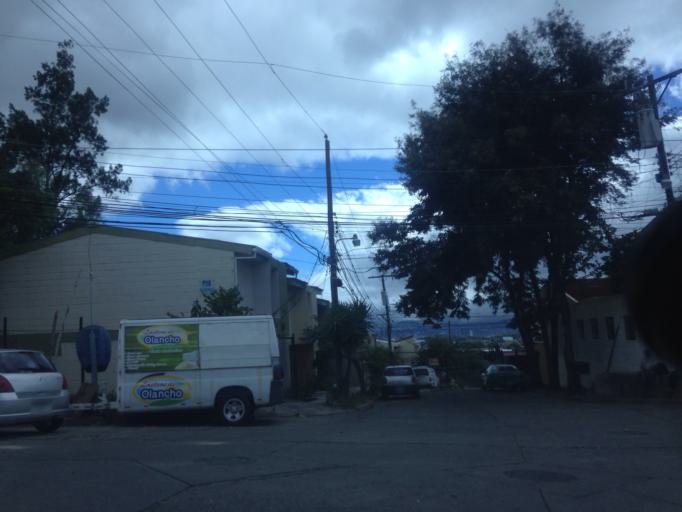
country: HN
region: Francisco Morazan
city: Tegucigalpa
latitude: 14.0553
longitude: -87.2368
